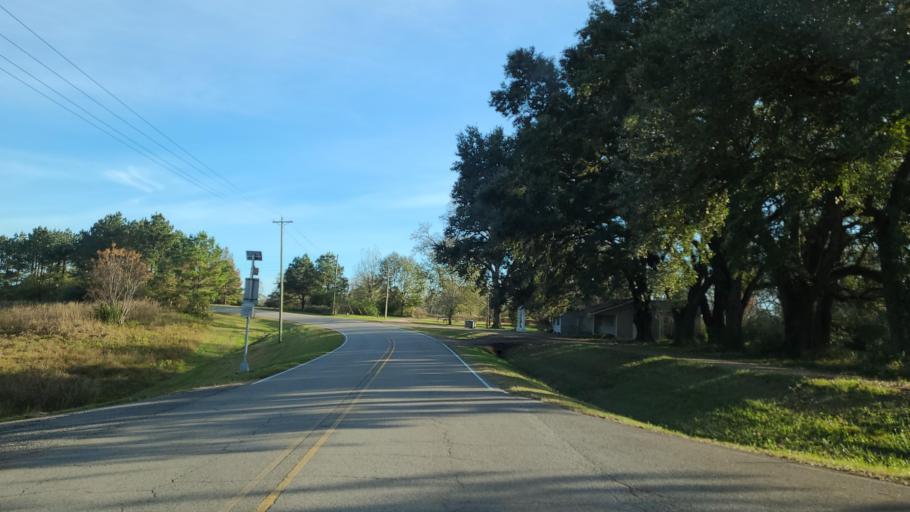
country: US
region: Mississippi
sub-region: Forrest County
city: Hattiesburg
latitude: 31.2151
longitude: -89.3026
